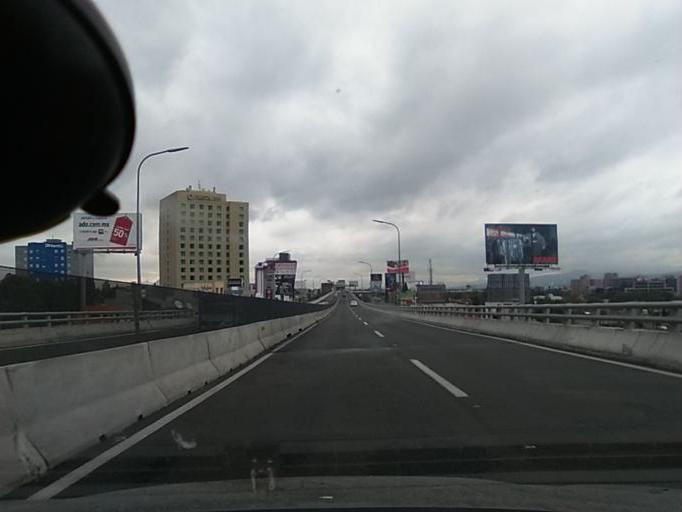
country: MX
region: Mexico City
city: Tlalpan
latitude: 19.3021
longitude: -99.1684
